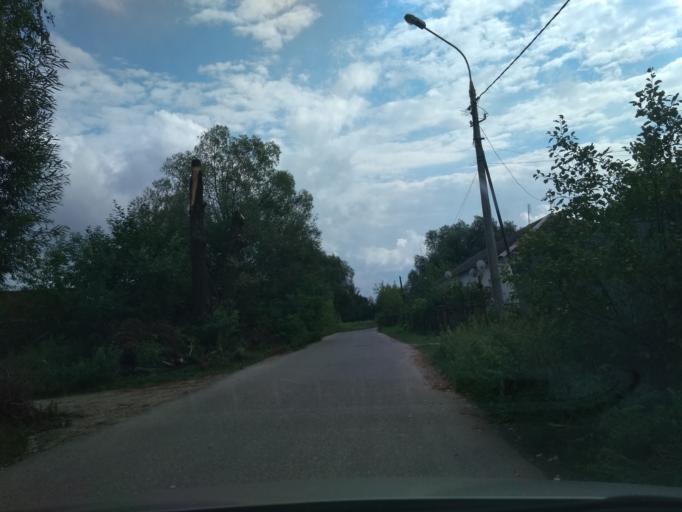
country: RU
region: Moskovskaya
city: Kabanovo
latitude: 55.7873
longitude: 38.9258
